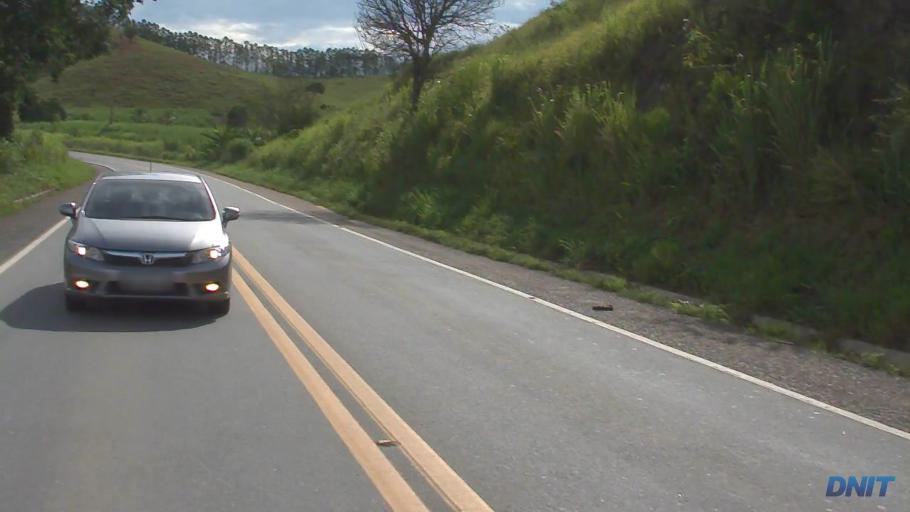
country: BR
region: Minas Gerais
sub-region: Belo Oriente
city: Belo Oriente
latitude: -19.1827
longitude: -42.2625
